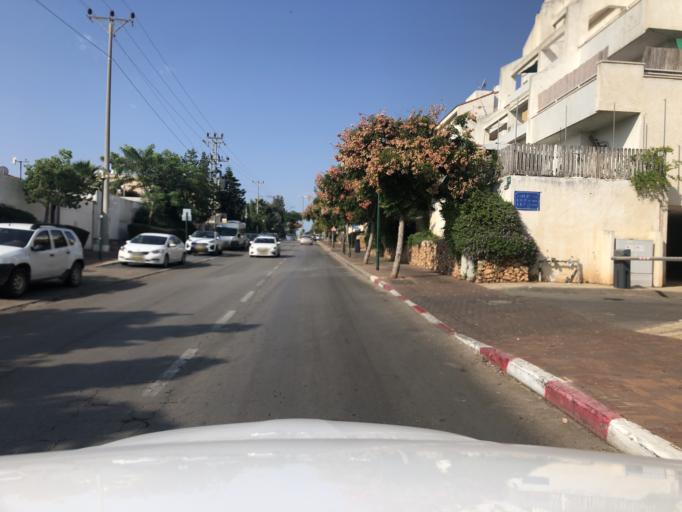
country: IL
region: Central District
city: Kfar Saba
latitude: 32.1833
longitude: 34.9122
